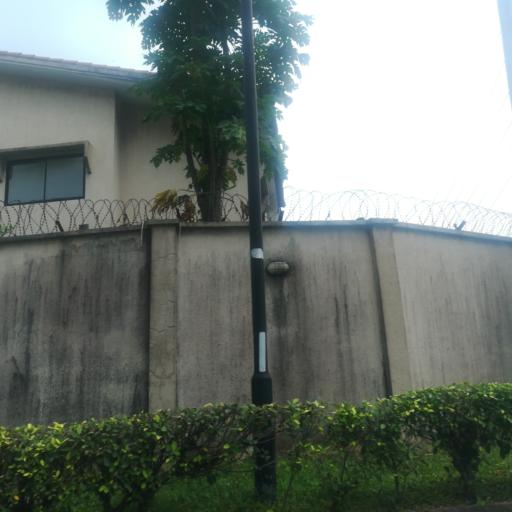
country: NG
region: Lagos
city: Ojota
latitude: 6.5739
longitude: 3.3901
